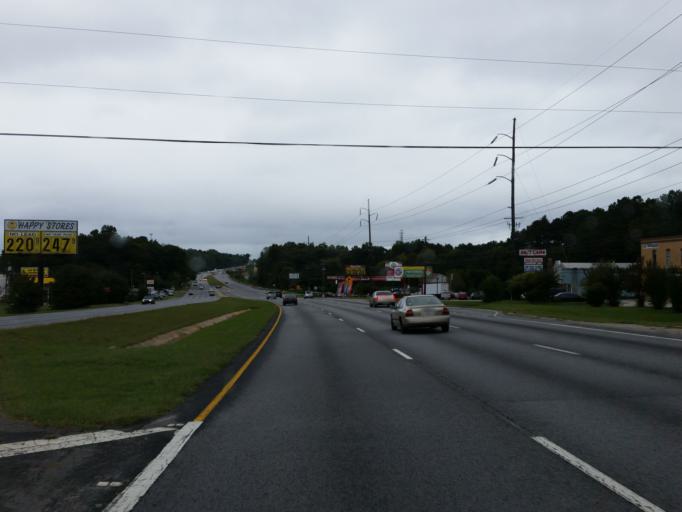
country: US
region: Georgia
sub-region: Clayton County
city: Jonesboro
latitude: 33.5465
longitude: -84.3694
